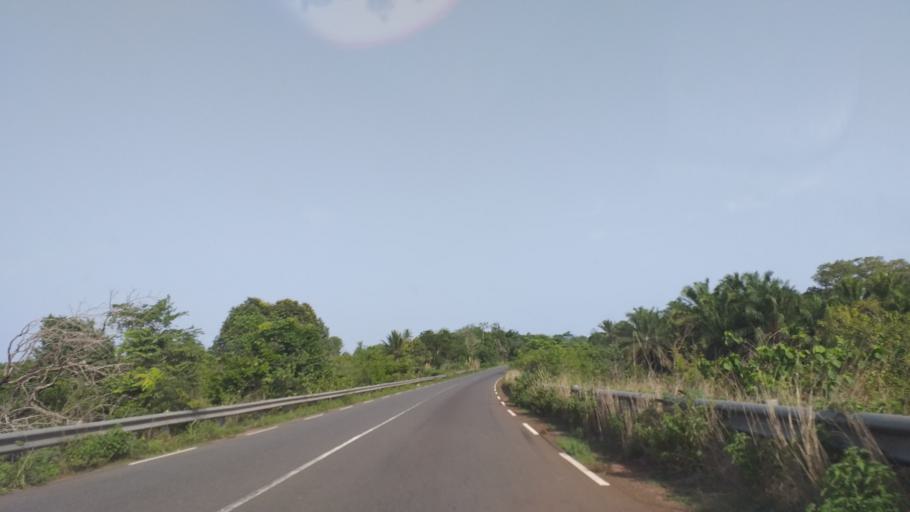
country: GN
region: Boke
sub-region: Boffa
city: Boffa
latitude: 10.2918
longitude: -14.1914
